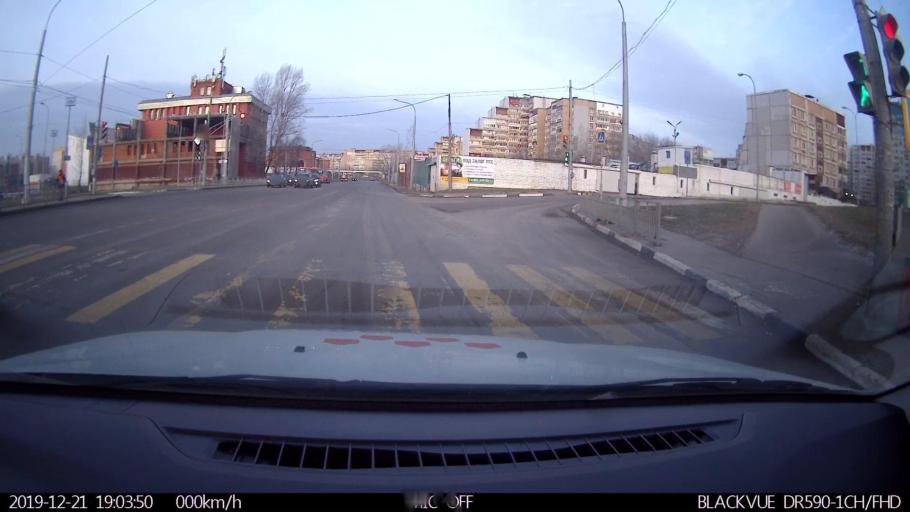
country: RU
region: Nizjnij Novgorod
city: Nizhniy Novgorod
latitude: 56.3398
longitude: 43.9441
